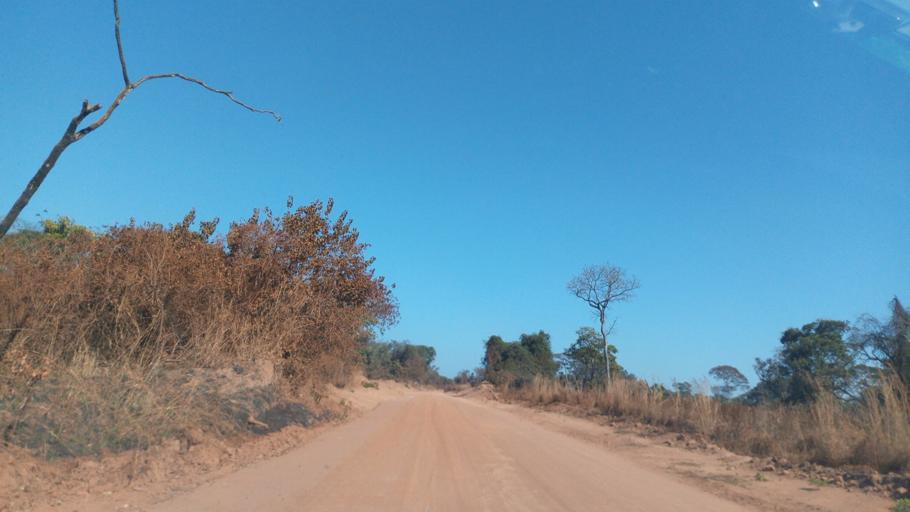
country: ZM
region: Luapula
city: Mwense
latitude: -10.7548
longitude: 28.3197
